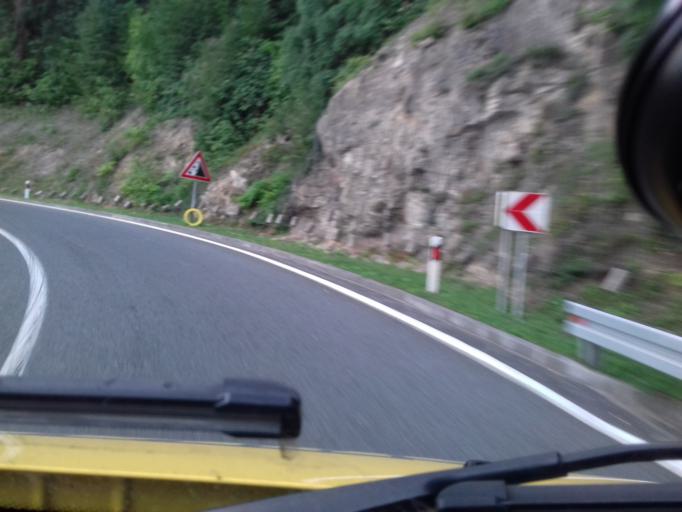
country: BA
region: Federation of Bosnia and Herzegovina
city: Ostrozac
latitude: 44.9019
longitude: 15.9315
